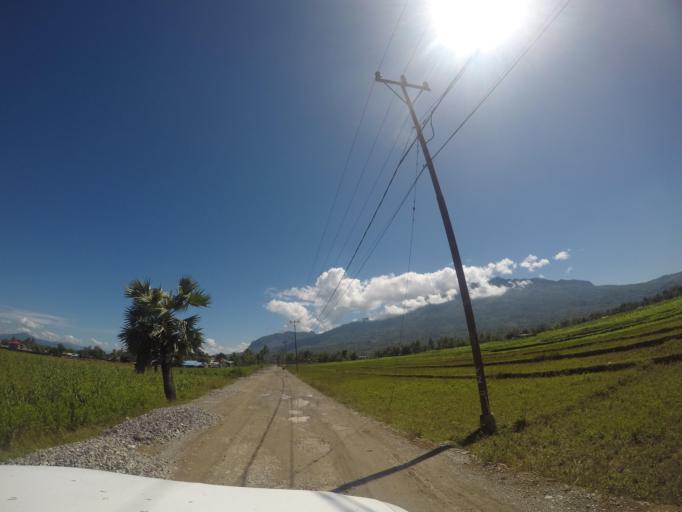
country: TL
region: Bobonaro
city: Maliana
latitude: -8.9864
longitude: 125.2097
